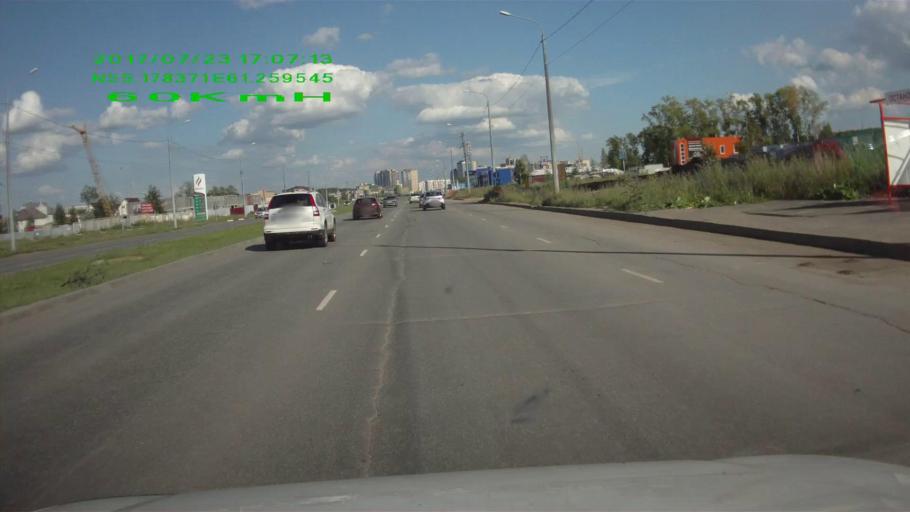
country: RU
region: Chelyabinsk
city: Roshchino
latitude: 55.1781
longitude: 61.2606
